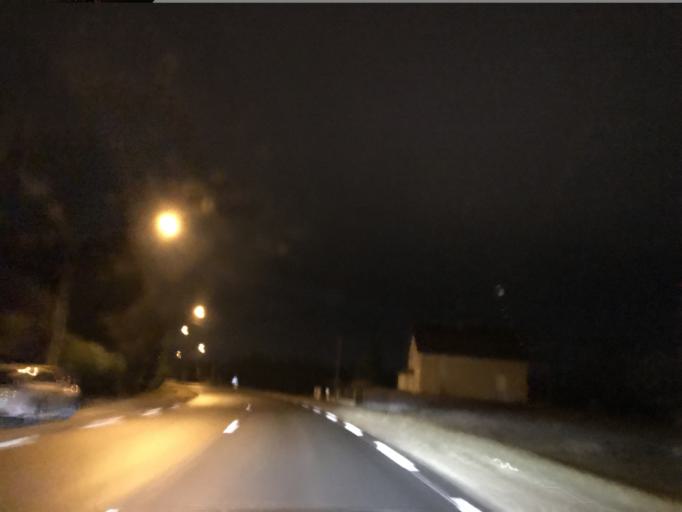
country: FR
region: Auvergne
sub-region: Departement de l'Allier
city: Abrest
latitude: 46.1011
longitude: 3.4286
